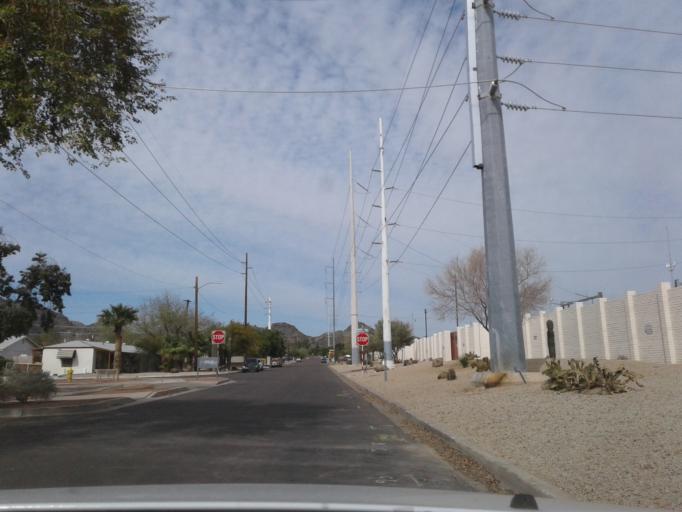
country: US
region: Arizona
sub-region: Maricopa County
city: Paradise Valley
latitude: 33.5737
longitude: -112.0609
